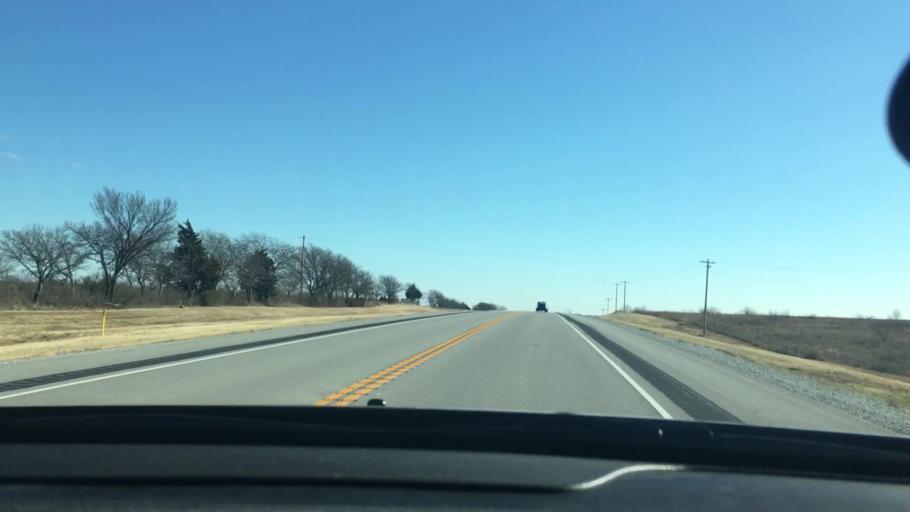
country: US
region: Oklahoma
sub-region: Love County
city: Marietta
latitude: 33.9400
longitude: -97.2395
